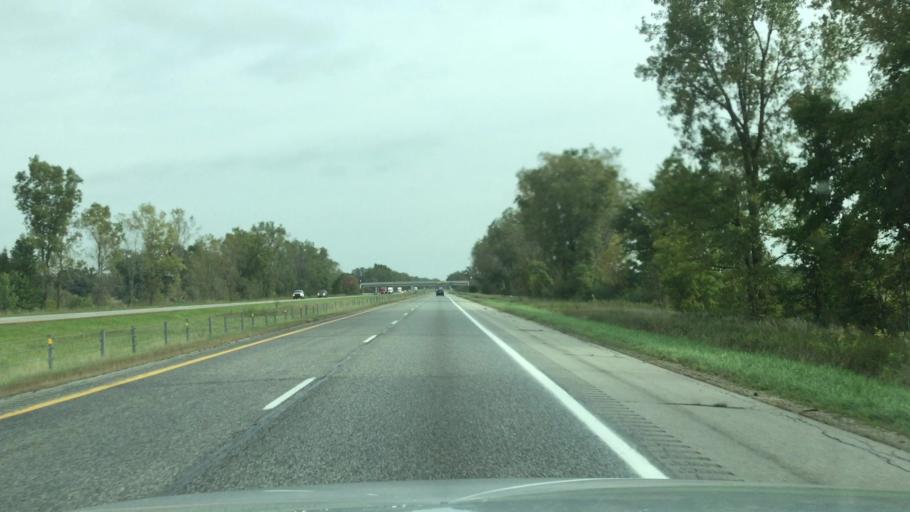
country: US
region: Michigan
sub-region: Shiawassee County
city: Perry
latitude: 42.8751
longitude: -84.1278
